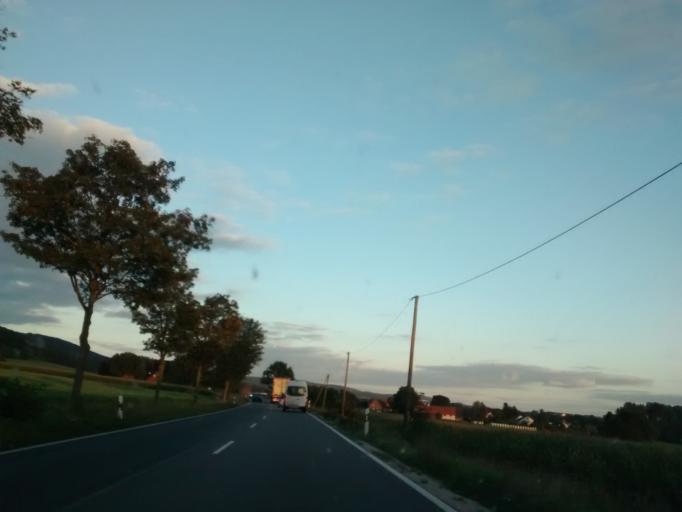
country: DE
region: North Rhine-Westphalia
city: Borgholzhausen
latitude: 52.0780
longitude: 8.3039
